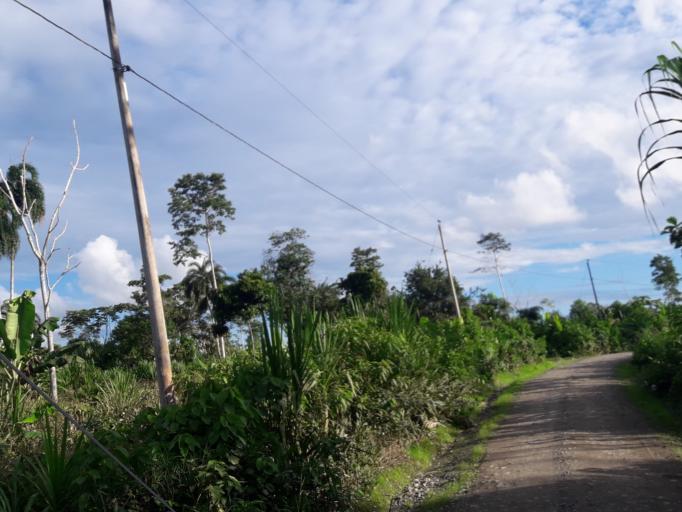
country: EC
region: Orellana
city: Boca Suno
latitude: -0.8843
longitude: -77.2965
